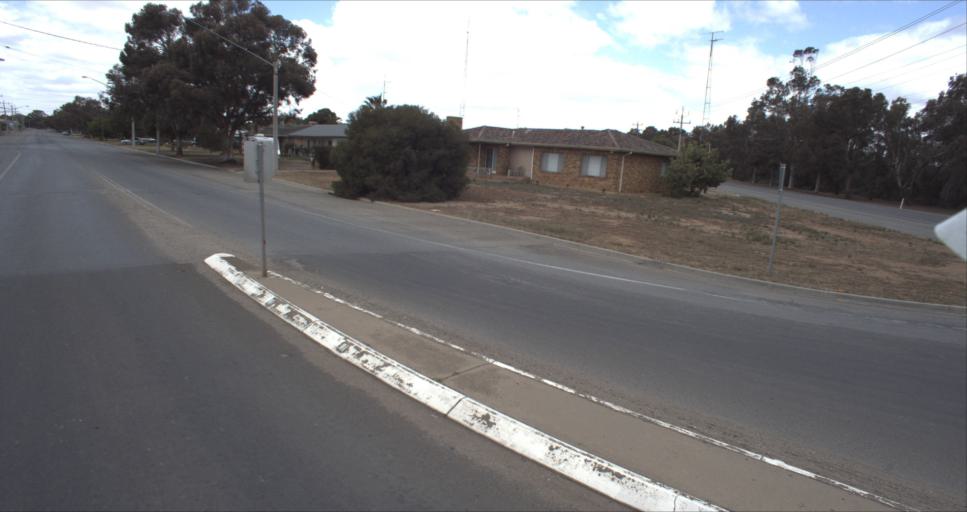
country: AU
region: New South Wales
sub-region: Leeton
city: Leeton
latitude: -34.5531
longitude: 146.3876
